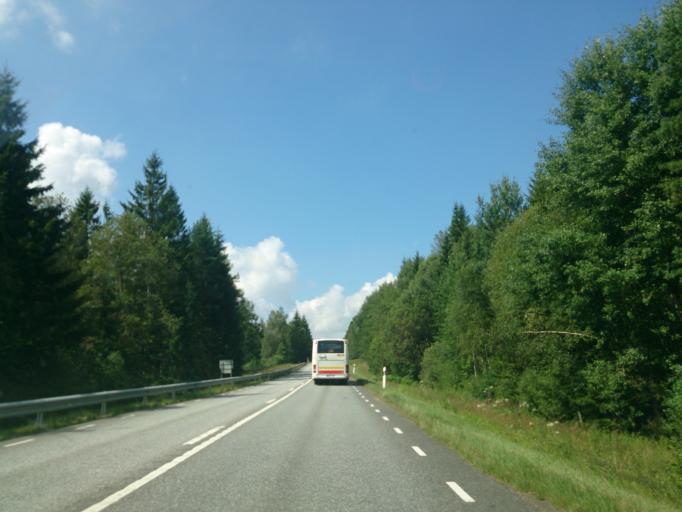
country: SE
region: Joenkoeping
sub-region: Varnamo Kommun
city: Bredaryd
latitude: 57.1719
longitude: 13.6980
